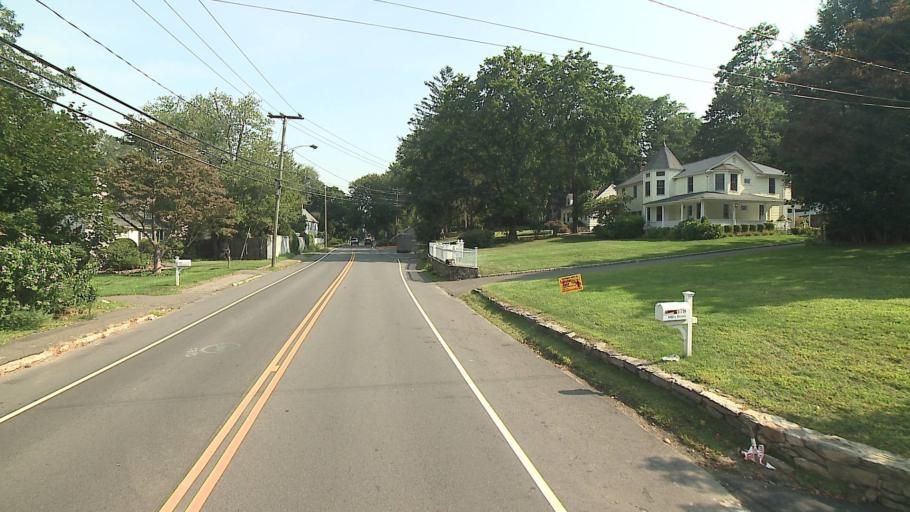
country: US
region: Connecticut
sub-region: Fairfield County
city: Westport
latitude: 41.1525
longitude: -73.3619
